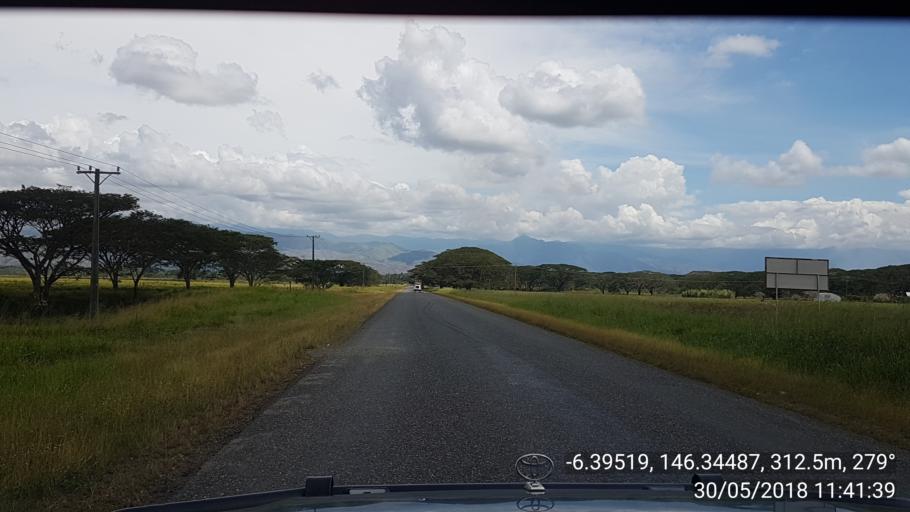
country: PG
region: Eastern Highlands
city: Kainantu
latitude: -6.3953
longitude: 146.3449
